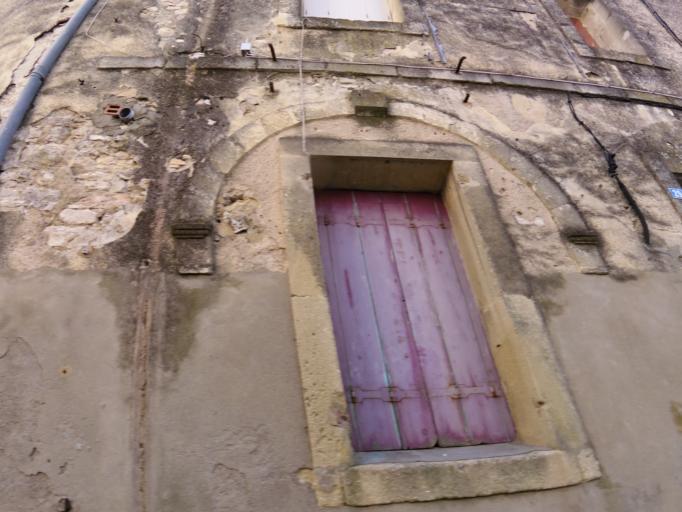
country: FR
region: Languedoc-Roussillon
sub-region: Departement du Gard
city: Sommieres
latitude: 43.8105
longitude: 4.0681
